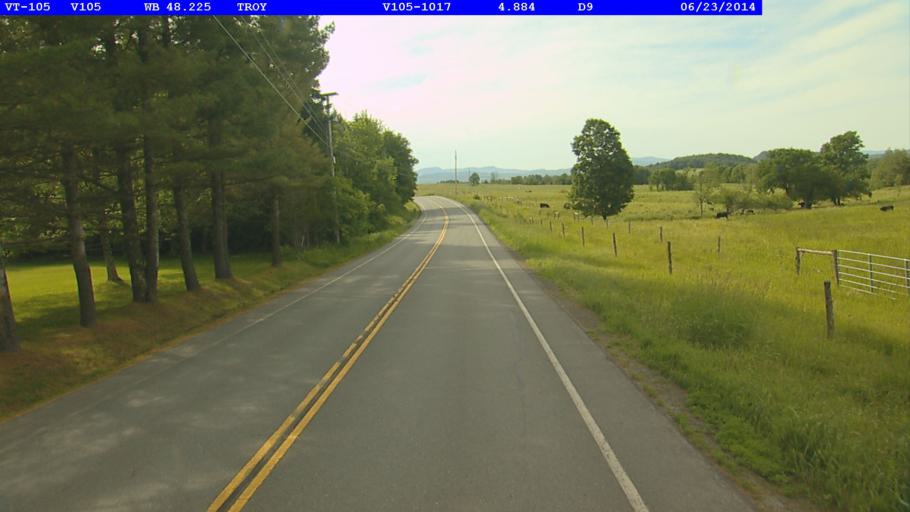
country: US
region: Vermont
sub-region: Orleans County
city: Newport
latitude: 44.9857
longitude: -72.3623
